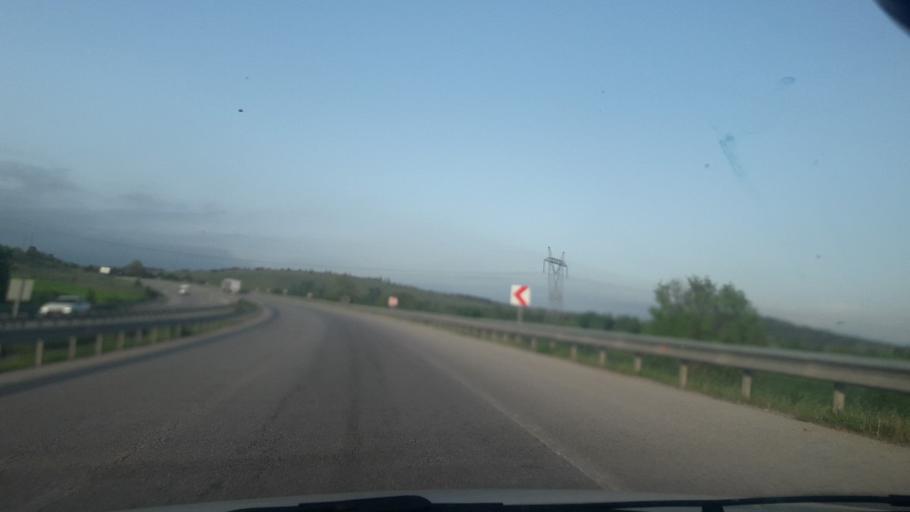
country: TR
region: Samsun
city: Ladik
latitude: 41.0024
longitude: 35.8359
